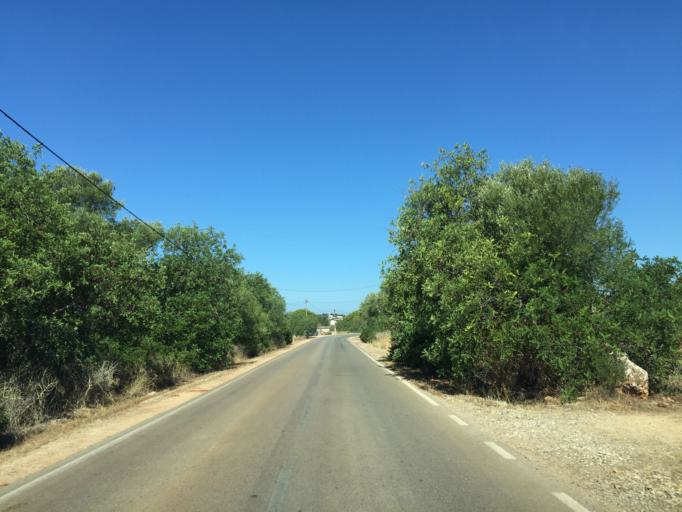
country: PT
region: Faro
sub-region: Loule
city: Almancil
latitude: 37.1114
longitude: -8.0726
